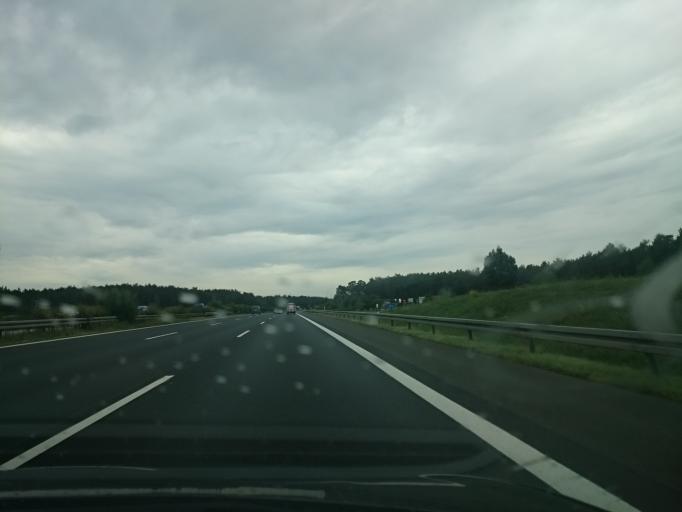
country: DE
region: Brandenburg
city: Borkheide
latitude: 52.2032
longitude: 12.8861
